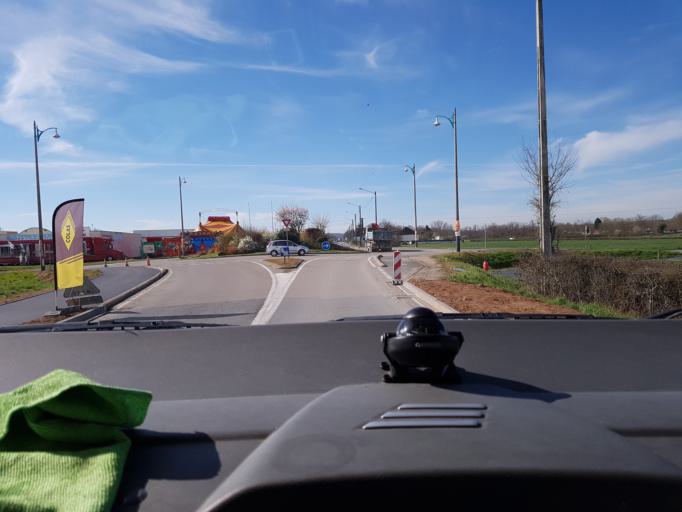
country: FR
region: Bourgogne
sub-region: Departement de Saone-et-Loire
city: Gueugnon
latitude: 46.5909
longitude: 4.0652
